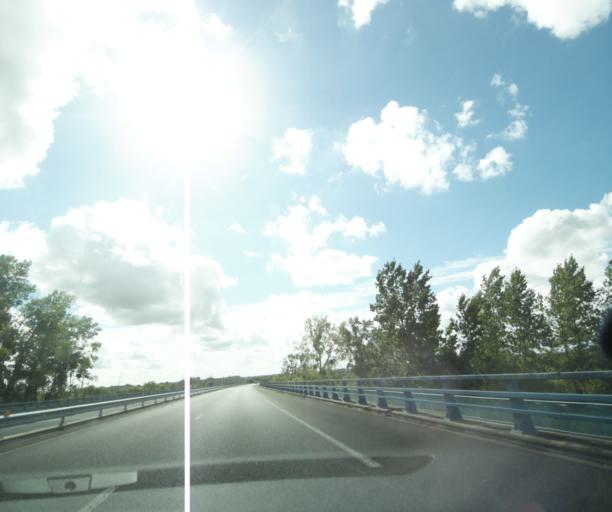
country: FR
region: Poitou-Charentes
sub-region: Departement de la Charente-Maritime
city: Bords
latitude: 45.8841
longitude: -0.7395
